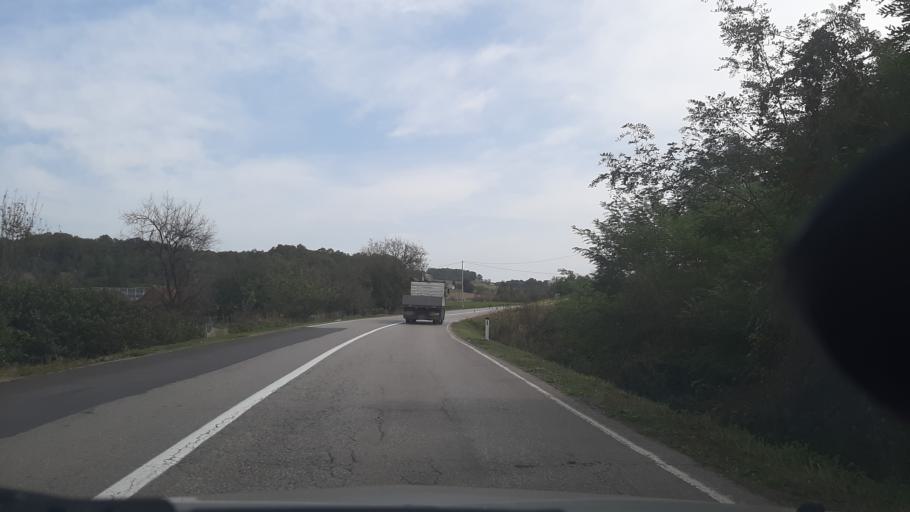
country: BA
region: Republika Srpska
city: Maglajani
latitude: 44.8648
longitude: 17.4318
